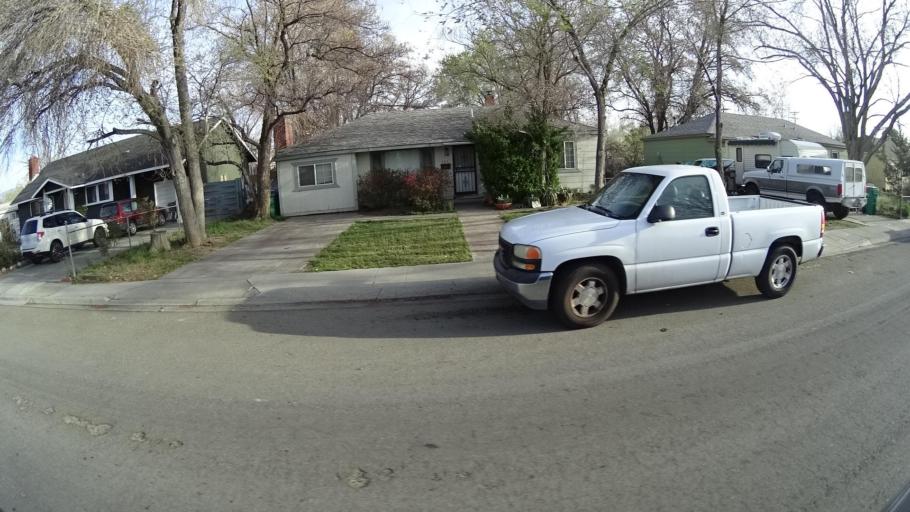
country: US
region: Nevada
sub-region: Washoe County
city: Reno
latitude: 39.5038
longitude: -119.7946
